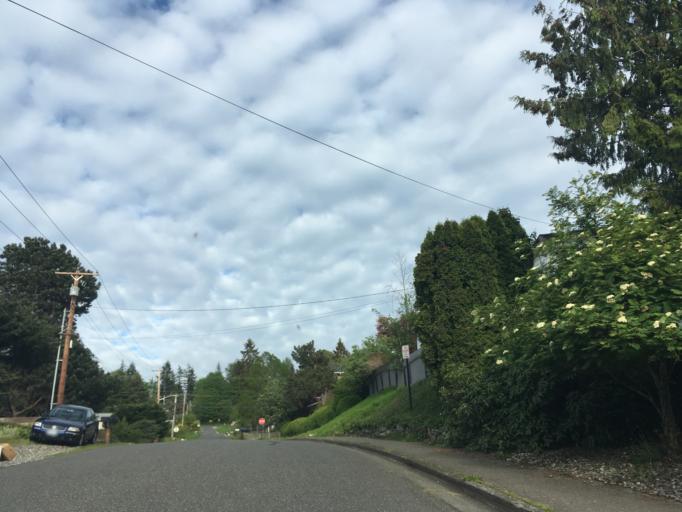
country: US
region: Washington
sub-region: Whatcom County
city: Geneva
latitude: 48.7617
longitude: -122.4384
